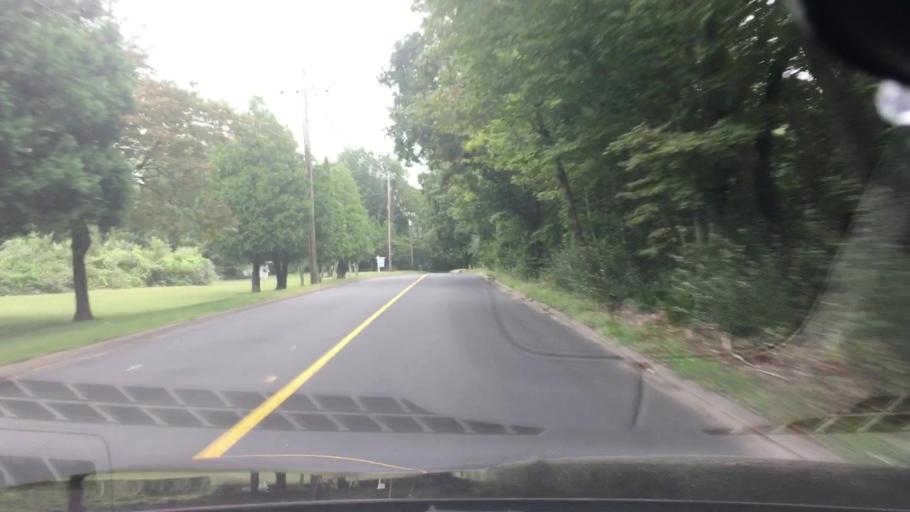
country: US
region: Connecticut
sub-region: New Haven County
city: Madison
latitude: 41.3282
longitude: -72.5905
